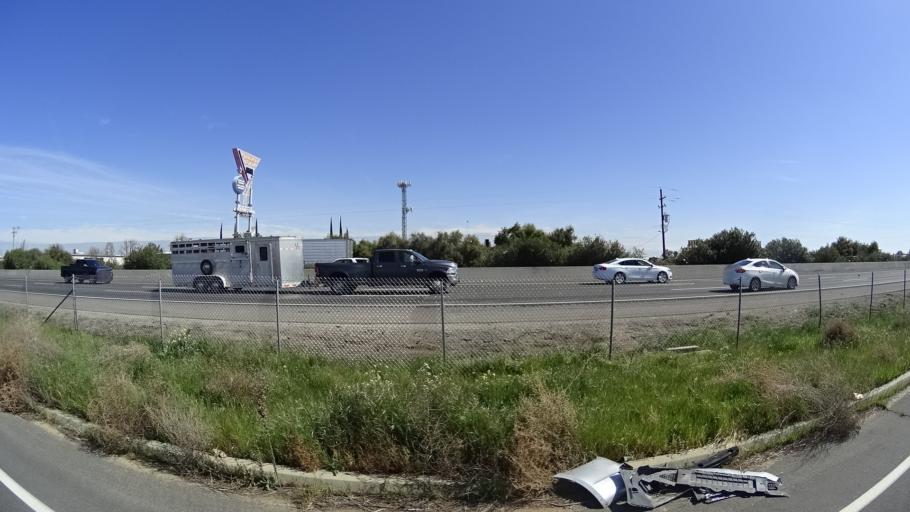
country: US
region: California
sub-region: Fresno County
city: West Park
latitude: 36.8127
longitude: -119.8936
